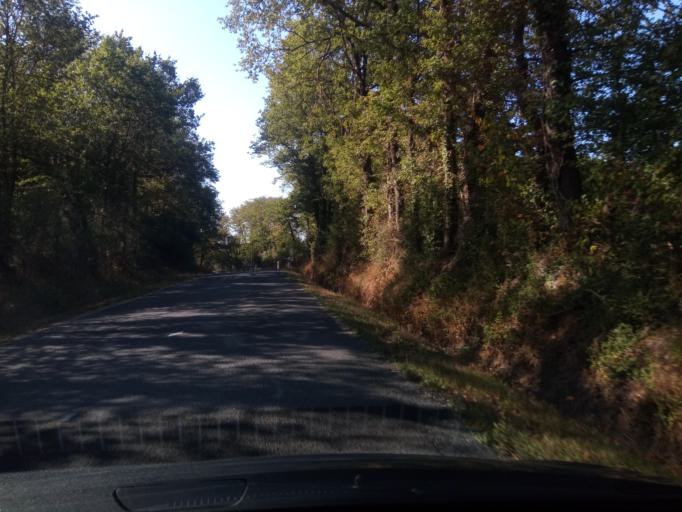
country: FR
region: Poitou-Charentes
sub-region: Departement de la Vienne
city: Saulge
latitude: 46.3457
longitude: 0.8698
